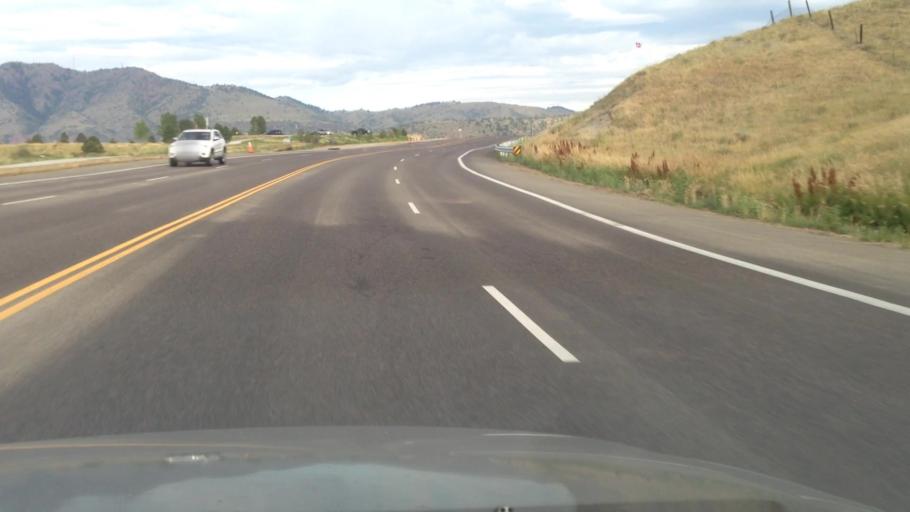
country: US
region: Colorado
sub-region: Jefferson County
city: West Pleasant View
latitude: 39.6803
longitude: -105.1659
